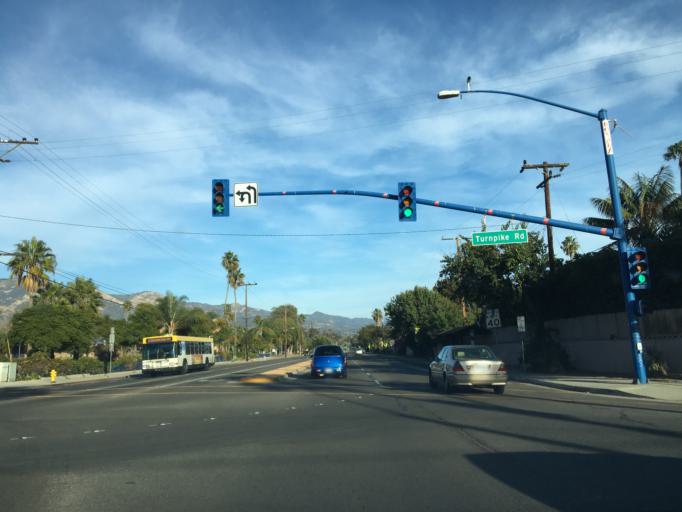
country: US
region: California
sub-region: Santa Barbara County
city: Goleta
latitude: 34.4365
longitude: -119.7897
